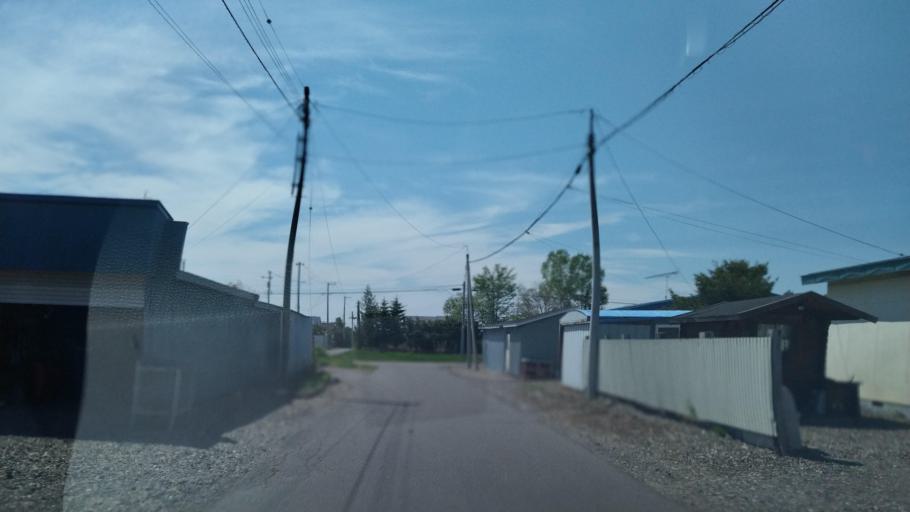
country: JP
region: Hokkaido
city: Otofuke
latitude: 43.2392
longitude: 143.2910
